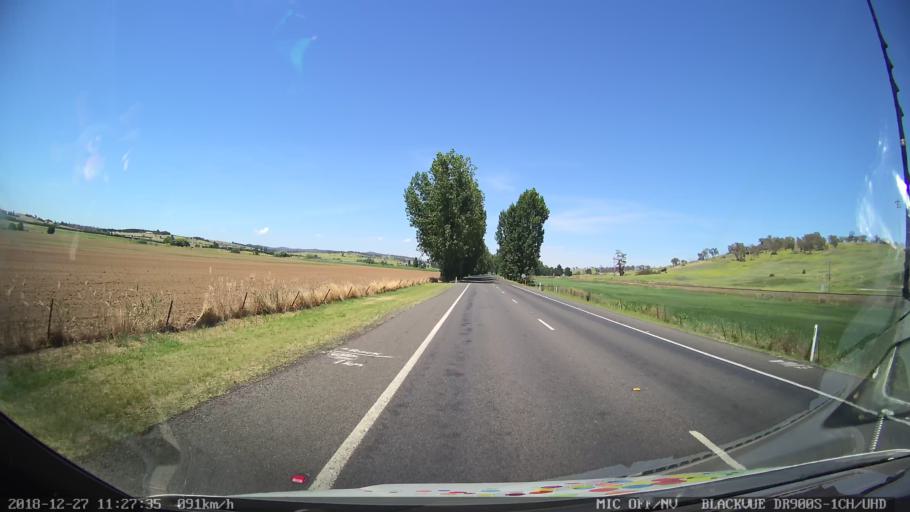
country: AU
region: New South Wales
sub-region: Bathurst Regional
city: Perthville
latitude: -33.4668
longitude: 149.5695
